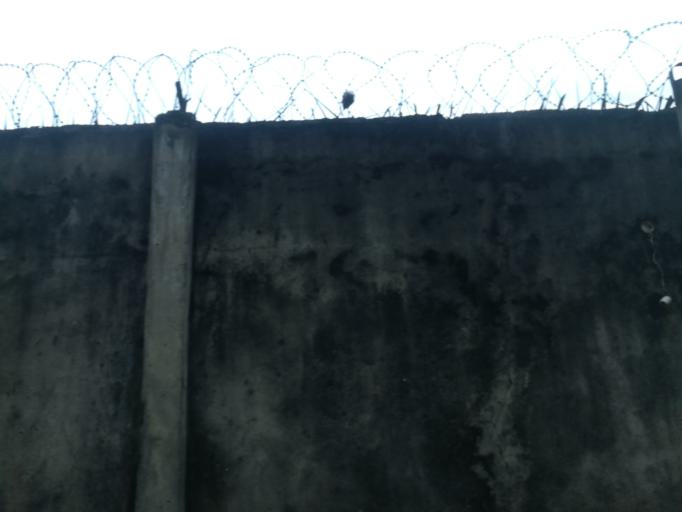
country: NG
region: Rivers
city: Port Harcourt
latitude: 4.7935
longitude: 6.9602
